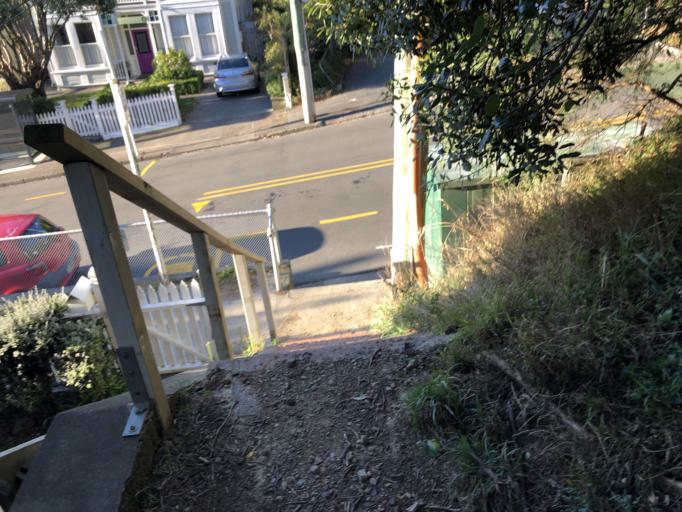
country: NZ
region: Wellington
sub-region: Wellington City
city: Wellington
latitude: -41.2992
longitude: 174.7881
